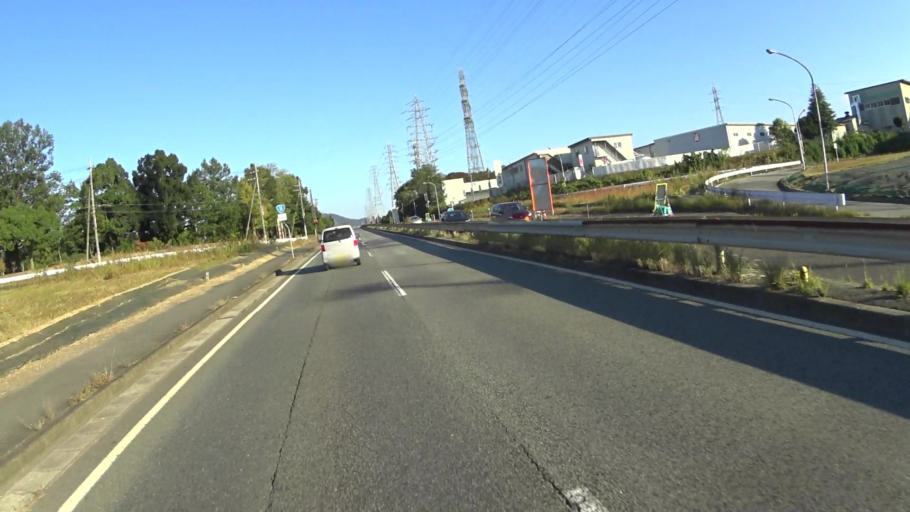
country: JP
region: Kyoto
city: Fukuchiyama
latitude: 35.2912
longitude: 135.1600
